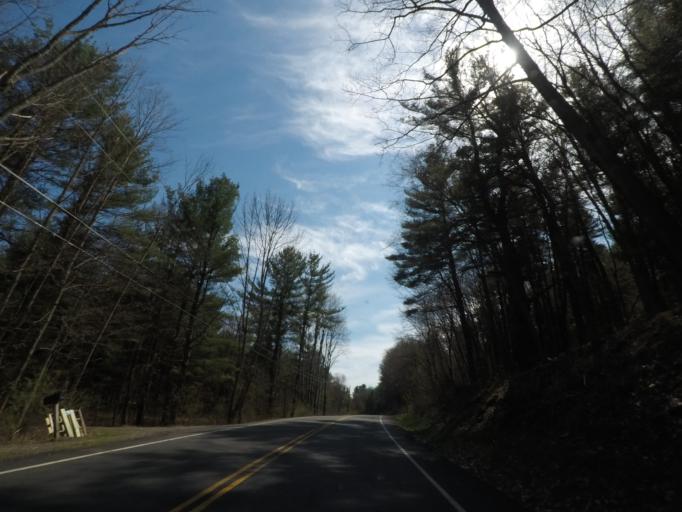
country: US
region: New York
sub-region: Columbia County
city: Chatham
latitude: 42.3755
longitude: -73.5299
